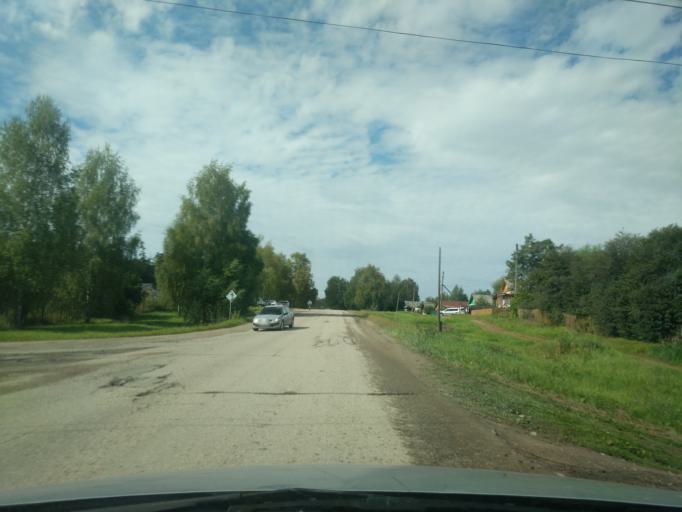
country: RU
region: Kostroma
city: Sudislavl'
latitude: 57.8793
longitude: 41.7226
